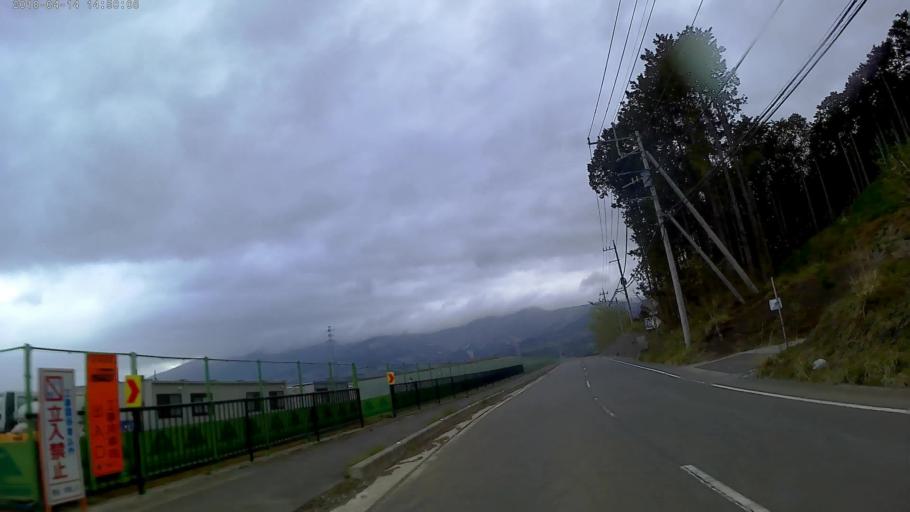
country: JP
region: Shizuoka
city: Gotemba
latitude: 35.3631
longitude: 138.9689
